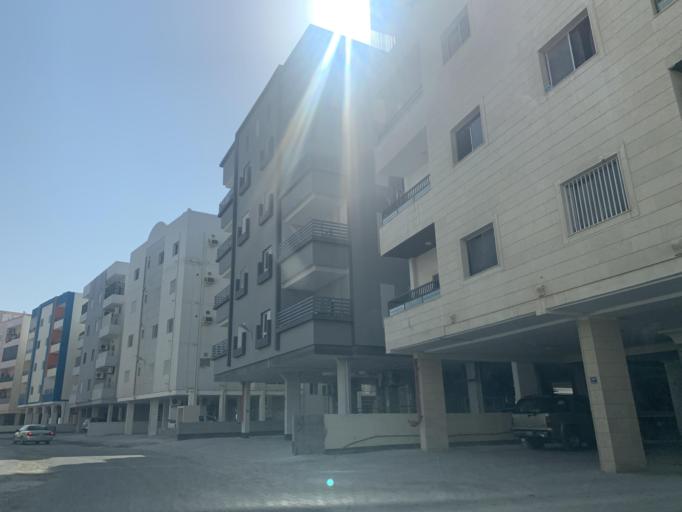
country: BH
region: Central Governorate
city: Madinat Hamad
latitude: 26.1311
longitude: 50.4885
